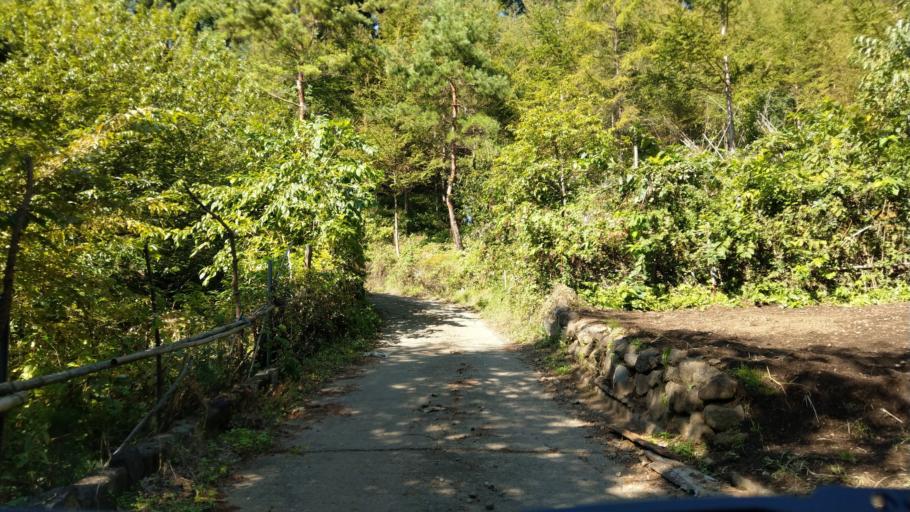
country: JP
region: Nagano
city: Komoro
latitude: 36.3591
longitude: 138.4316
